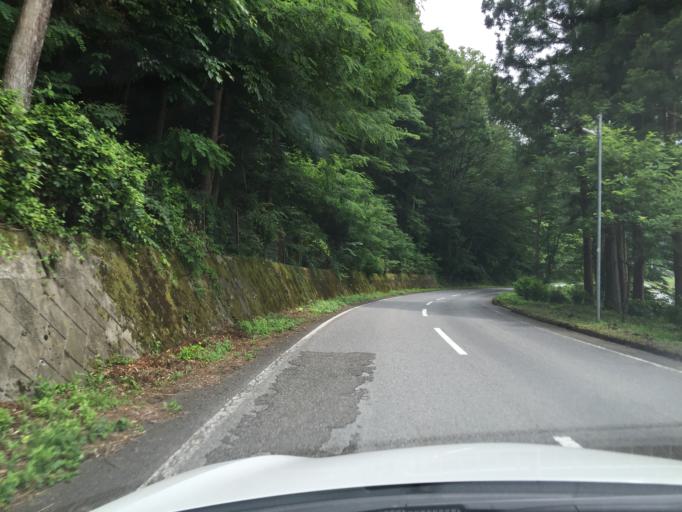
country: JP
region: Fukushima
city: Miharu
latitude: 37.3015
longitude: 140.5412
